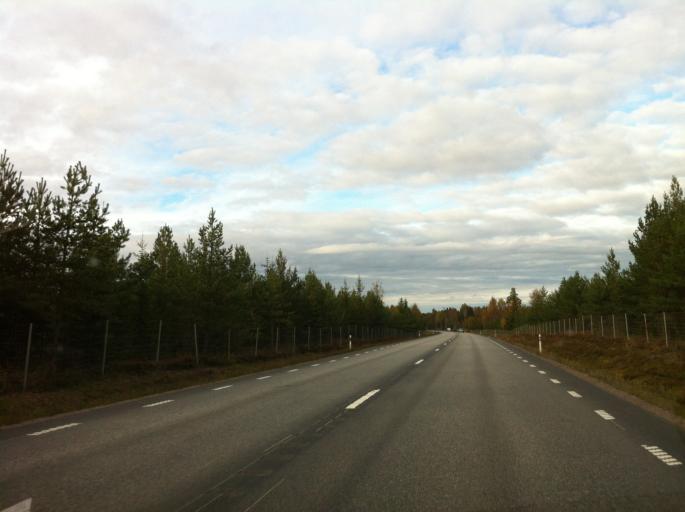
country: SE
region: OErebro
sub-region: Askersunds Kommun
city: Asbro
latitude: 58.9495
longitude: 15.0319
